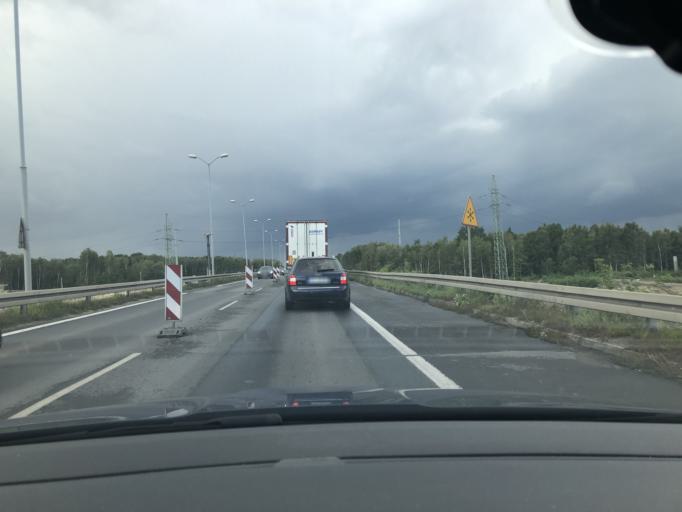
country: PL
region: Silesian Voivodeship
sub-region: Katowice
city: Murcki
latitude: 50.2289
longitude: 19.0568
